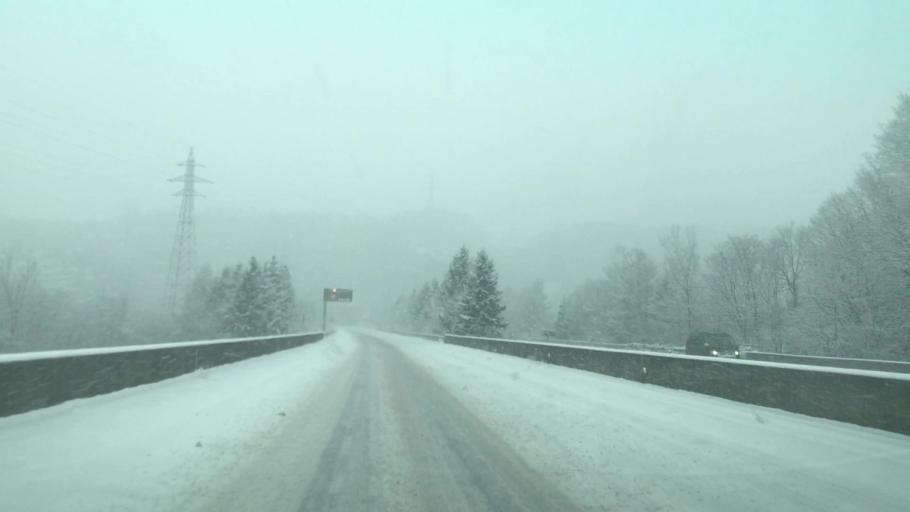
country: JP
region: Hokkaido
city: Muroran
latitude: 42.4266
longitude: 141.0945
